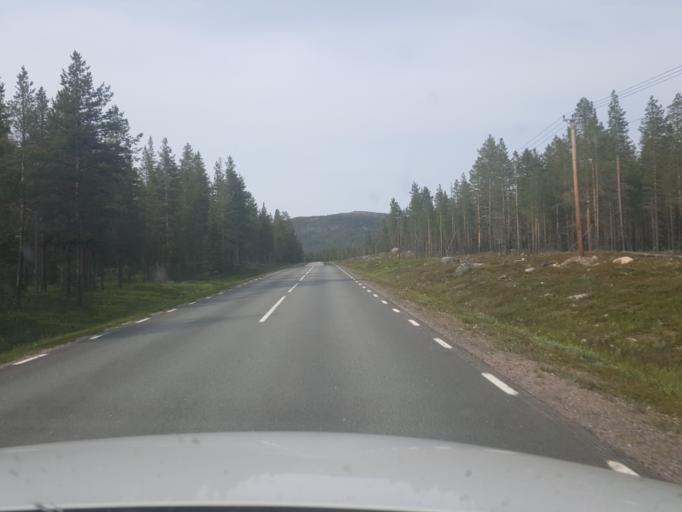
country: SE
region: Norrbotten
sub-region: Arjeplogs Kommun
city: Arjeplog
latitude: 65.8562
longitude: 18.0416
